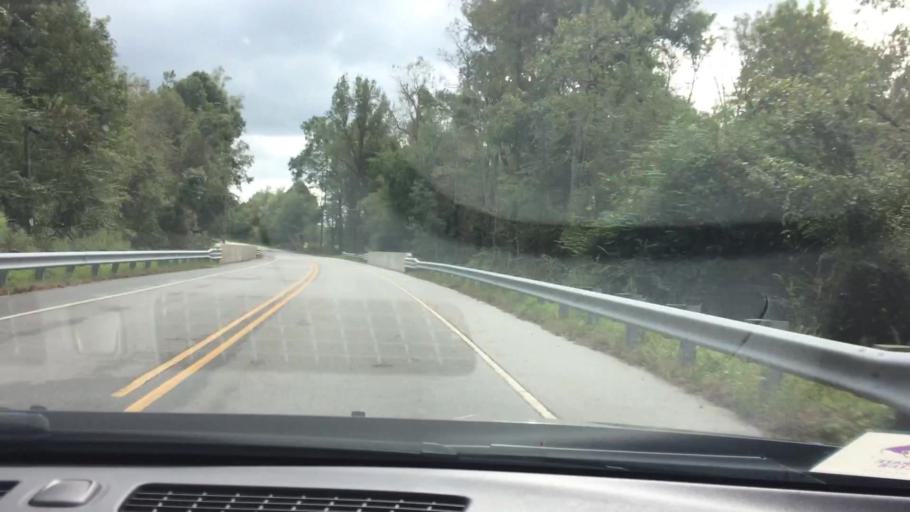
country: US
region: North Carolina
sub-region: Greene County
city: Maury
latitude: 35.5329
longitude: -77.5455
